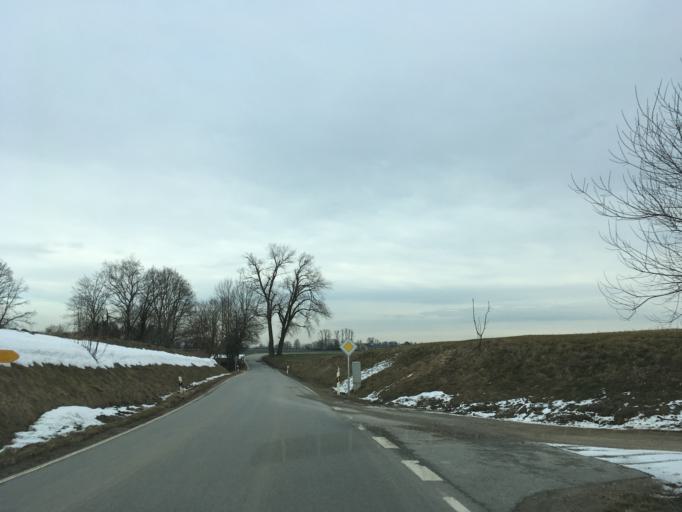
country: DE
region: Bavaria
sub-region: Upper Bavaria
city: Kraiburg am Inn
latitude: 48.1676
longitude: 12.4147
